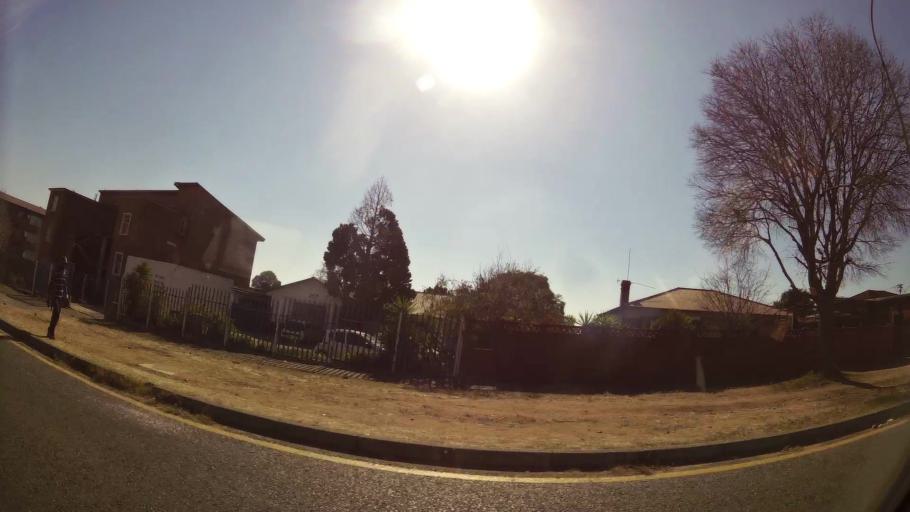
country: ZA
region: Gauteng
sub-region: City of Johannesburg Metropolitan Municipality
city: Johannesburg
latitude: -26.2602
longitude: 28.0336
